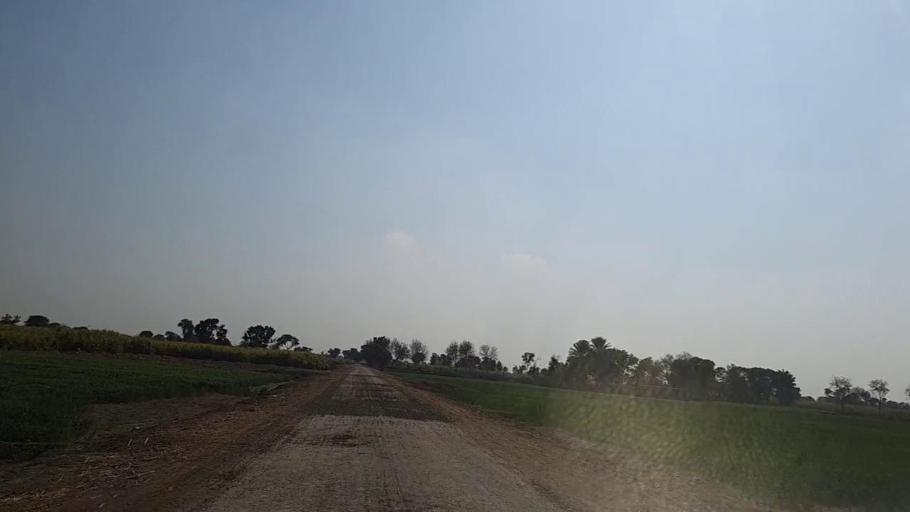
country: PK
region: Sindh
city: Daur
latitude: 26.4392
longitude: 68.2332
